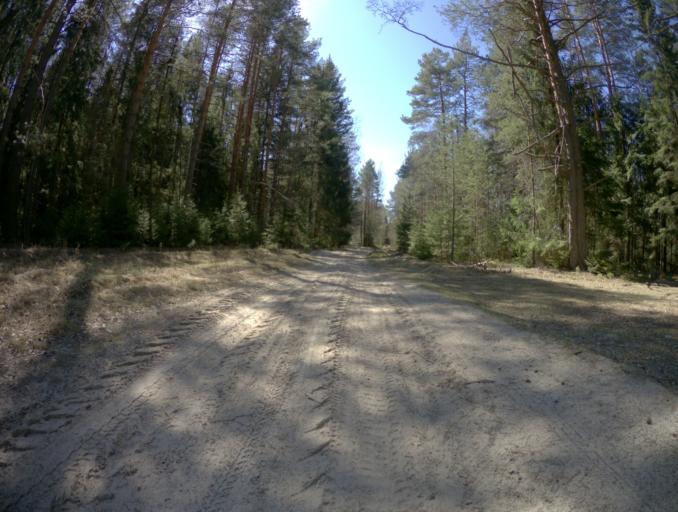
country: RU
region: Vladimir
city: Golovino
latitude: 55.9036
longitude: 40.4398
